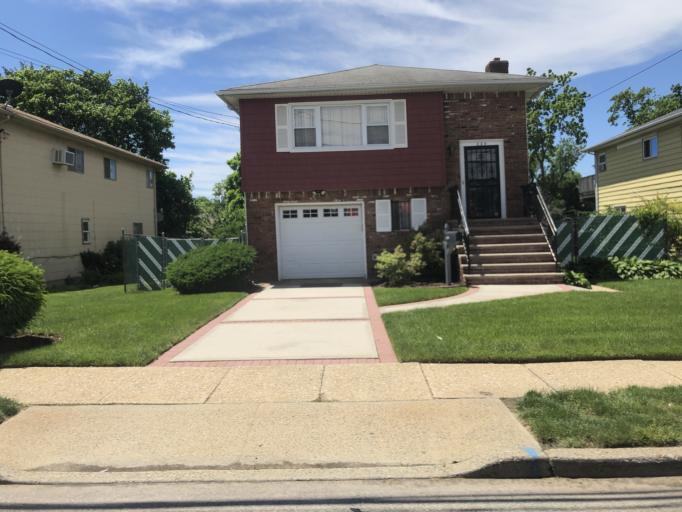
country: US
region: New York
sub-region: Nassau County
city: Freeport
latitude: 40.6696
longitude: -73.5774
